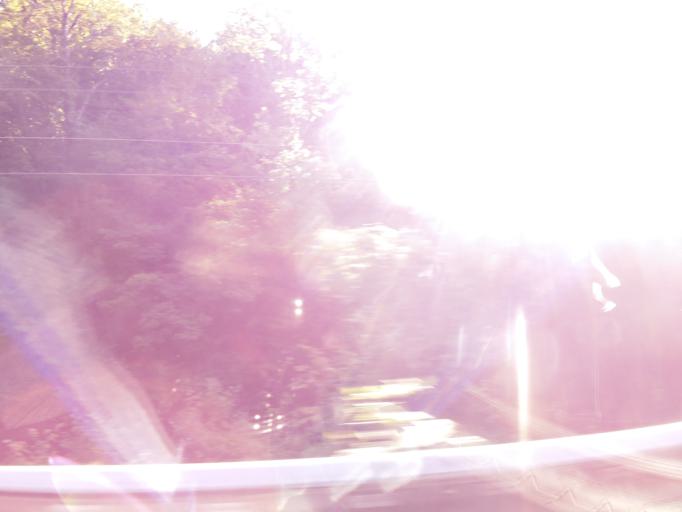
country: US
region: Tennessee
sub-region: Union County
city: Condon
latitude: 36.1881
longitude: -83.8147
